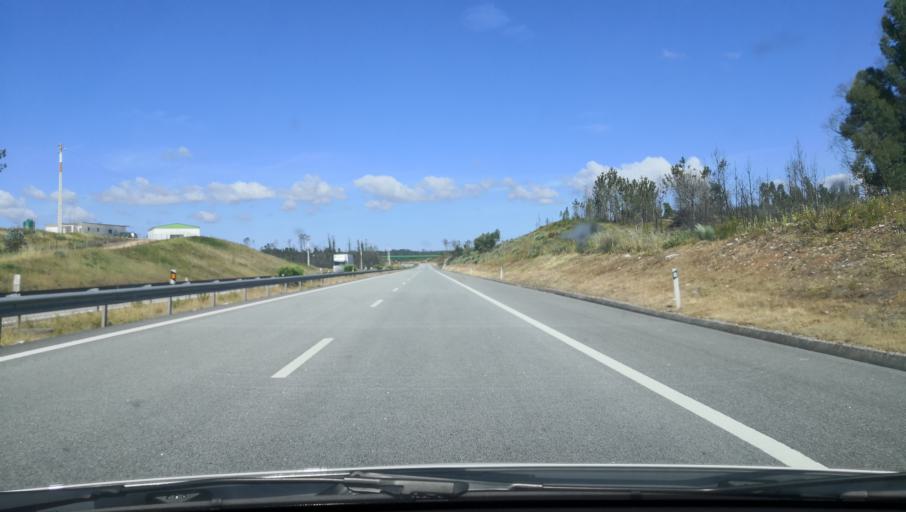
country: PT
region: Coimbra
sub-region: Cantanhede
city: Cantanhede
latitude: 40.2849
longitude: -8.5603
